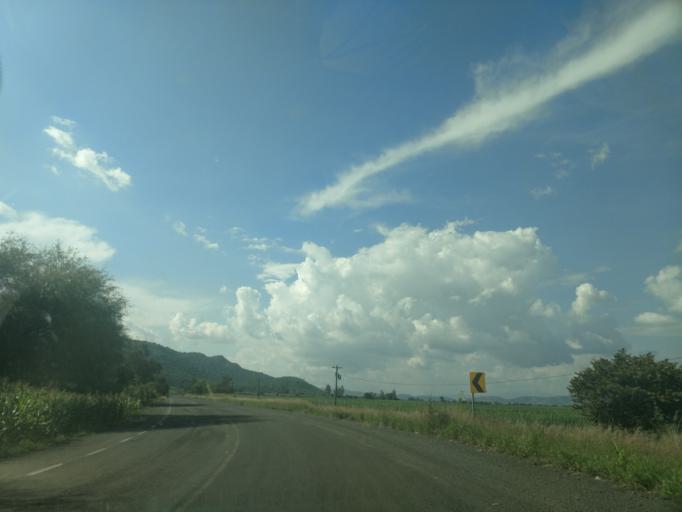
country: MX
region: Jalisco
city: Antonio Escobedo
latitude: 20.8532
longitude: -104.0284
